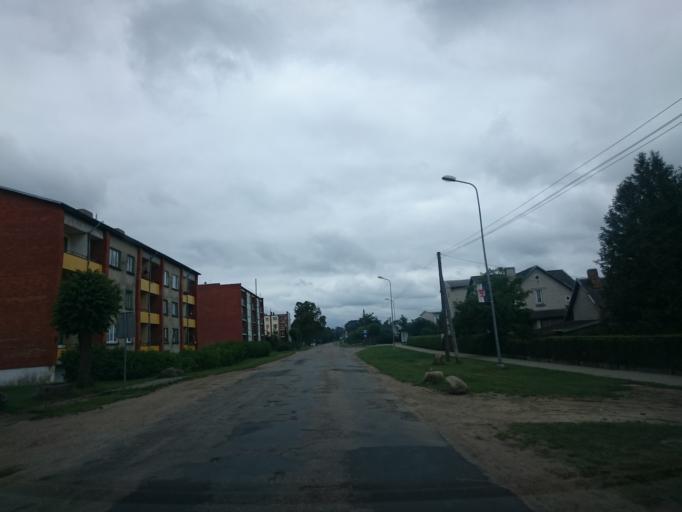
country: LV
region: Pavilostas
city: Pavilosta
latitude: 56.8840
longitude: 21.2002
